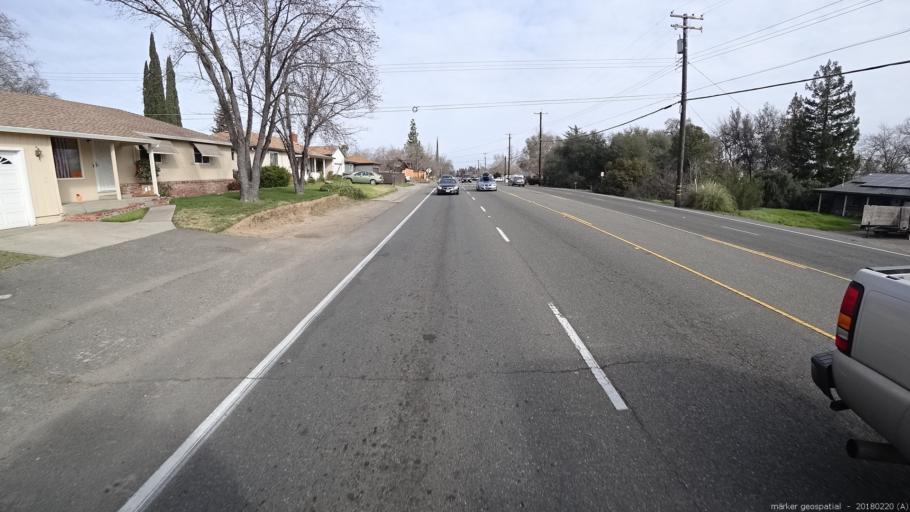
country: US
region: California
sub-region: Sacramento County
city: Orangevale
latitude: 38.6867
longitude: -121.2255
